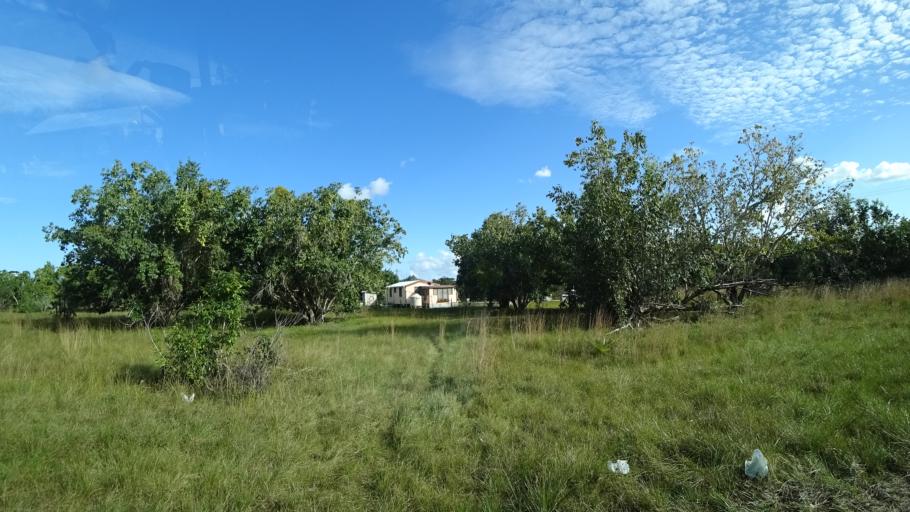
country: BZ
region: Belize
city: Belize City
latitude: 17.5574
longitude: -88.3995
